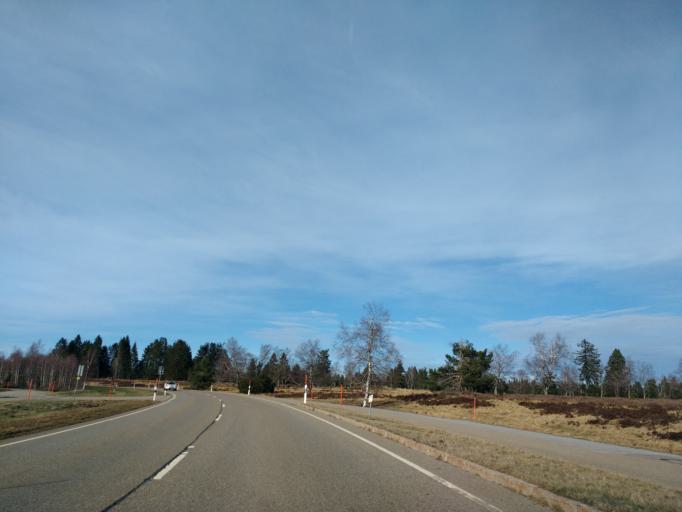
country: DE
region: Baden-Wuerttemberg
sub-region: Freiburg Region
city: Bad Peterstal-Griesbach
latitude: 48.4925
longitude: 8.2674
